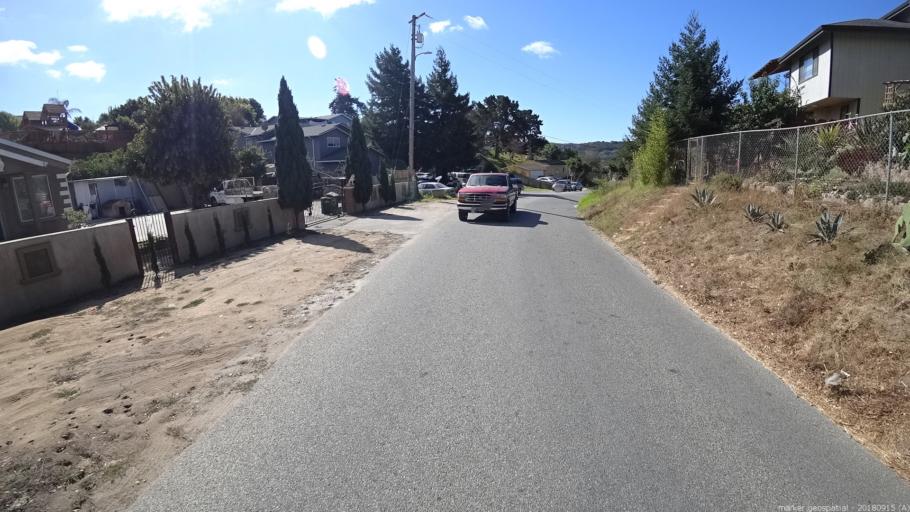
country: US
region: California
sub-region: Monterey County
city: Las Lomas
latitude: 36.8704
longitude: -121.7324
